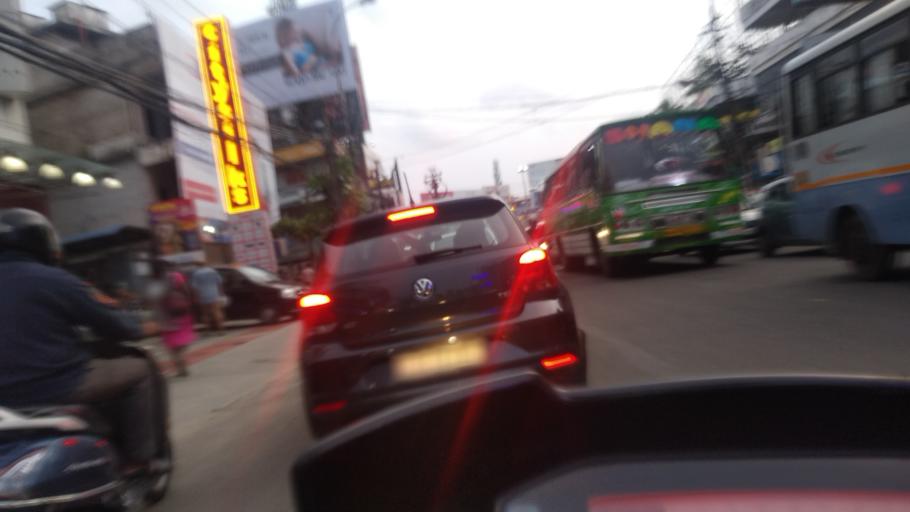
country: IN
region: Kerala
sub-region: Ernakulam
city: Elur
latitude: 10.0032
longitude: 76.3075
